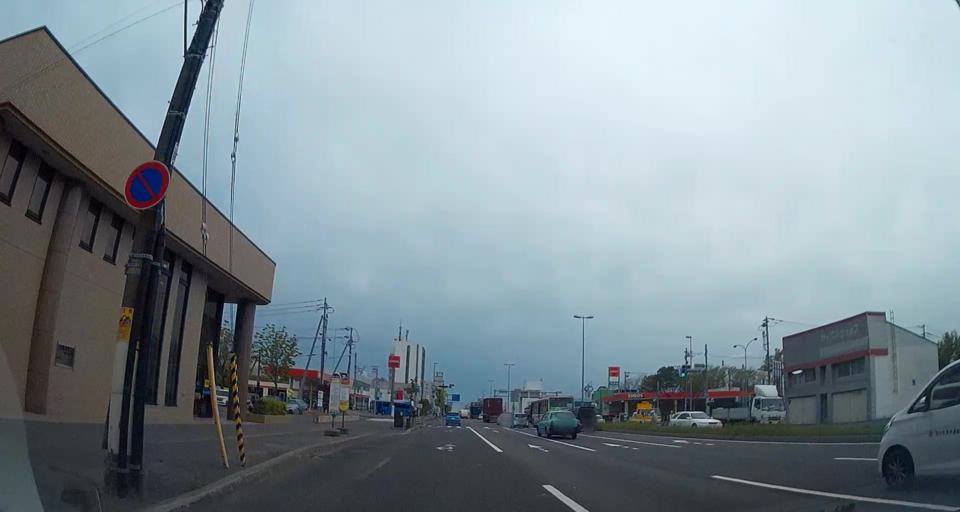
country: JP
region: Hokkaido
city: Tomakomai
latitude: 42.6394
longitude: 141.6126
